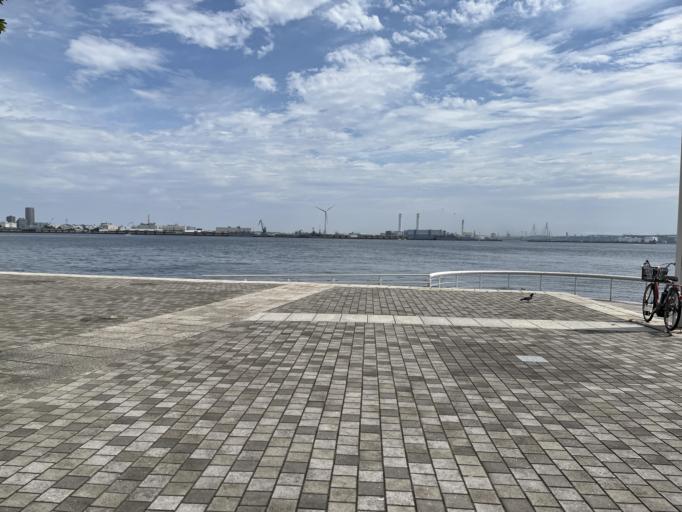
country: JP
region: Kanagawa
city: Yokohama
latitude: 35.4587
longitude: 139.6382
